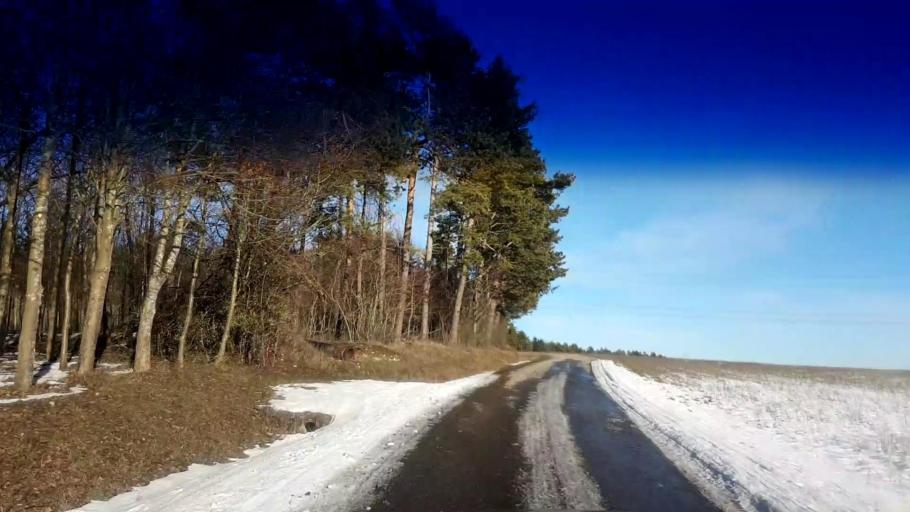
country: DE
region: Bavaria
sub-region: Upper Franconia
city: Heiligenstadt
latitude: 49.8401
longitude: 11.1014
